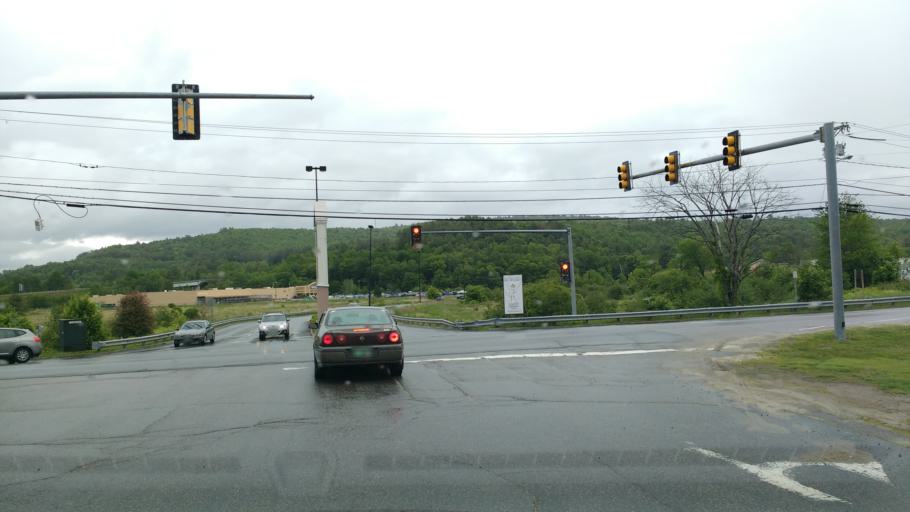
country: US
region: New Hampshire
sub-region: Grafton County
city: Littleton
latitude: 44.3057
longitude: -71.8039
